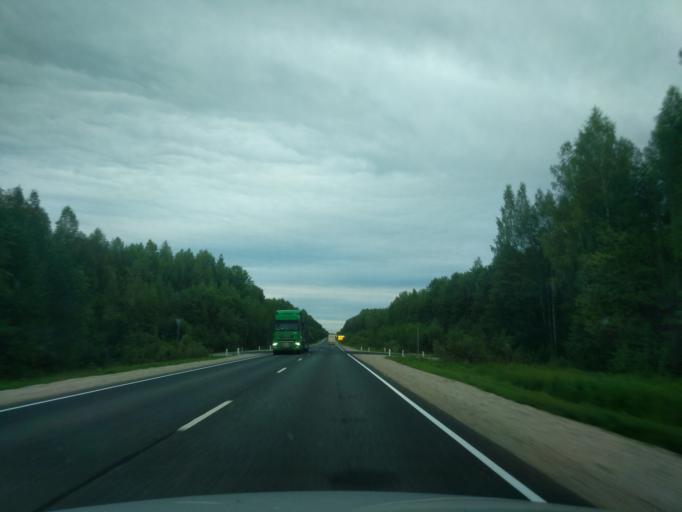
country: RU
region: Kostroma
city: Ponazyrevo
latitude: 58.3234
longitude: 46.5212
